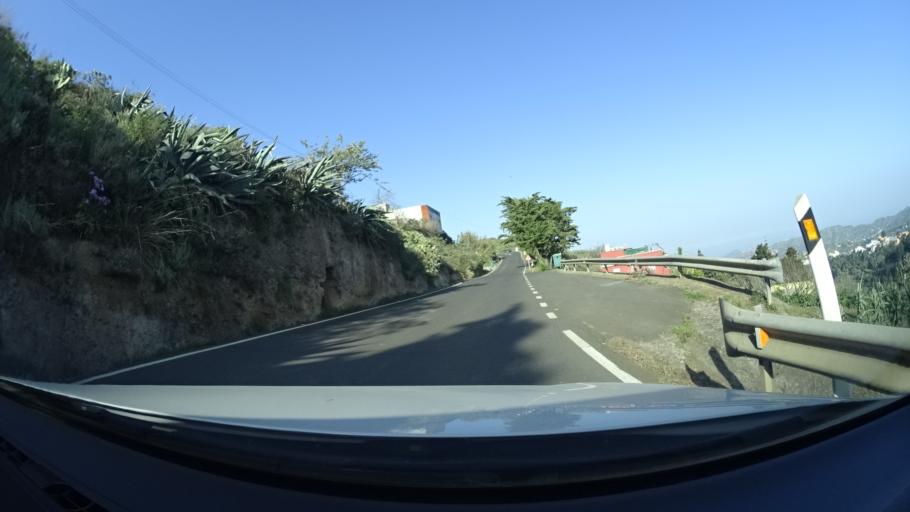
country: ES
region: Canary Islands
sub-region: Provincia de Las Palmas
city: Valleseco
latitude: 28.0283
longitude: -15.5538
